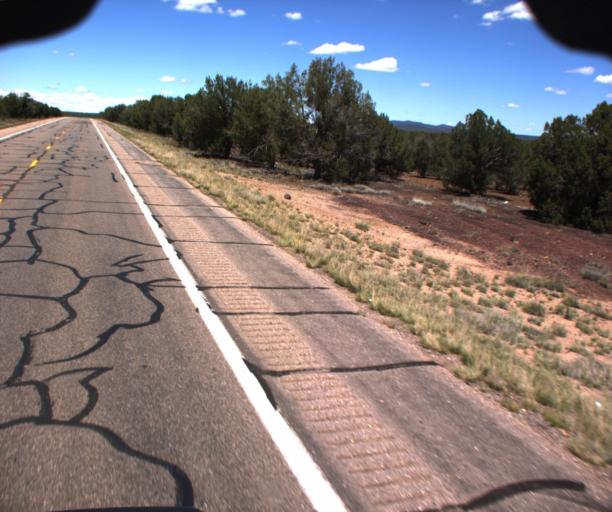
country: US
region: Arizona
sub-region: Yavapai County
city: Paulden
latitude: 35.0304
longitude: -112.3943
